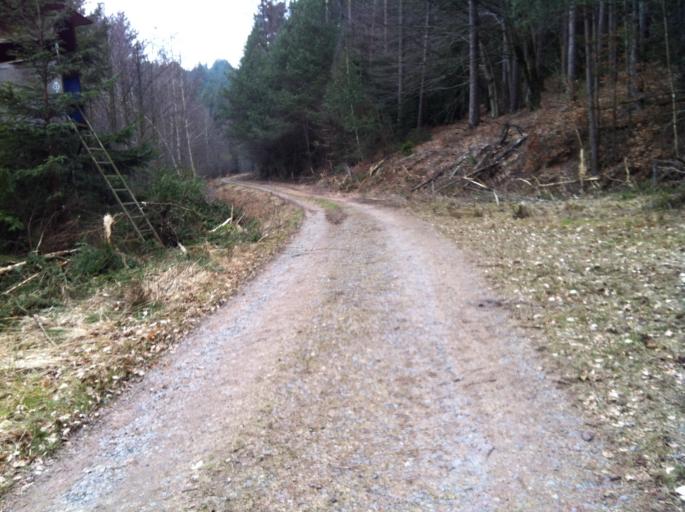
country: DE
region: Hesse
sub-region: Regierungsbezirk Darmstadt
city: Wald-Michelbach
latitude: 49.6275
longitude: 8.8932
